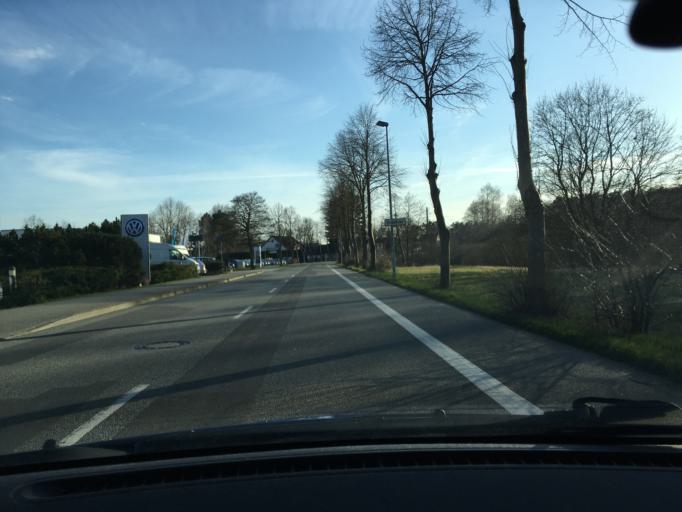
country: DE
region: Mecklenburg-Vorpommern
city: Feldstadt
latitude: 53.5962
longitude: 11.4143
